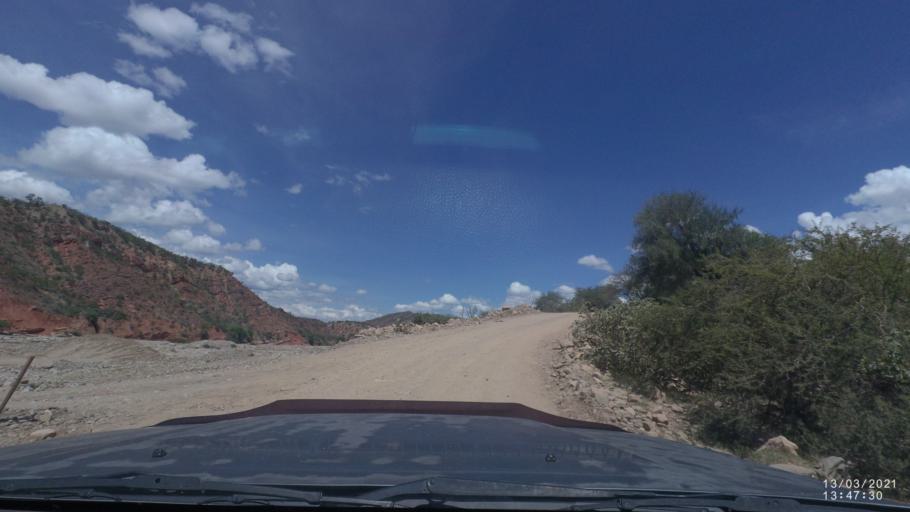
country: BO
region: Cochabamba
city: Cliza
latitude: -17.9338
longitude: -65.8679
